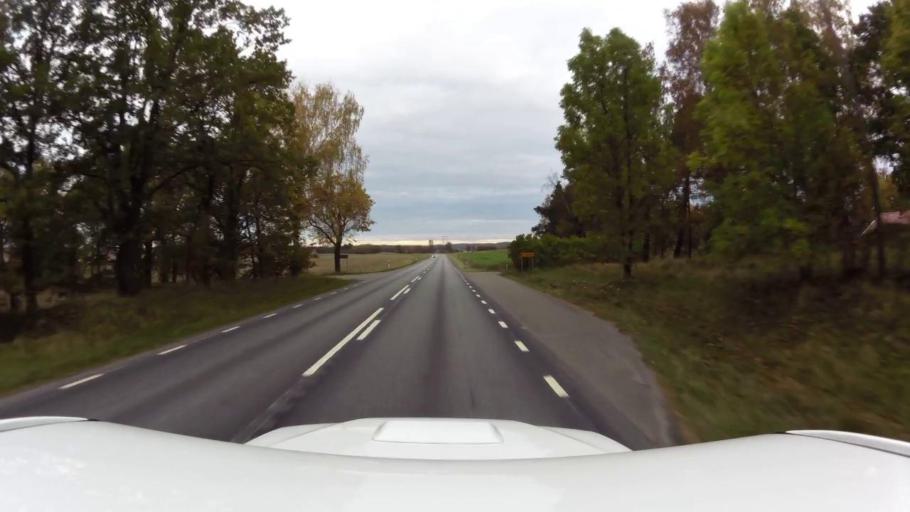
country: SE
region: OEstergoetland
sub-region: Linkopings Kommun
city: Ljungsbro
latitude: 58.5092
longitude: 15.4473
